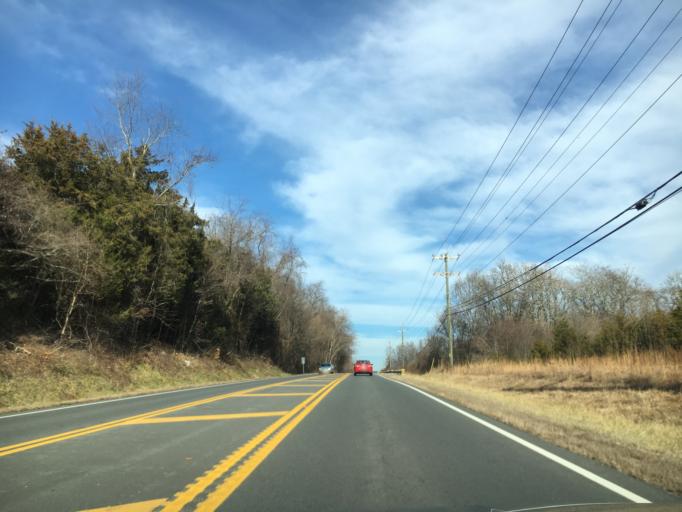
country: US
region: Virginia
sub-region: Fauquier County
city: Warrenton
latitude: 38.6620
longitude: -77.9236
